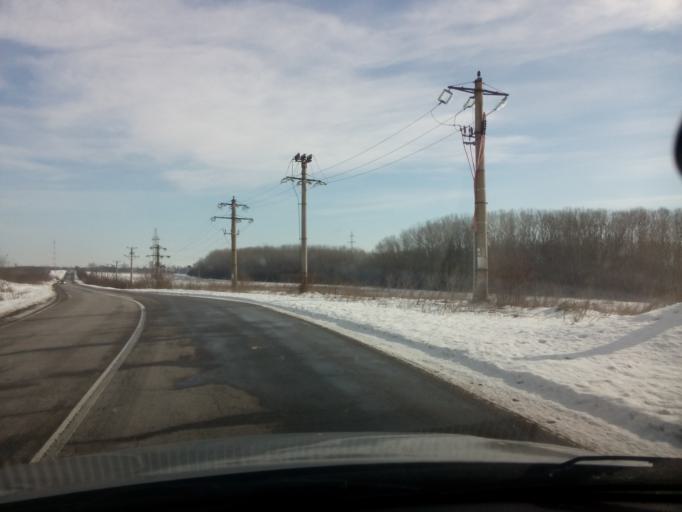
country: RO
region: Calarasi
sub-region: Comuna Budesti
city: Budesti
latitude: 44.2320
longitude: 26.4749
